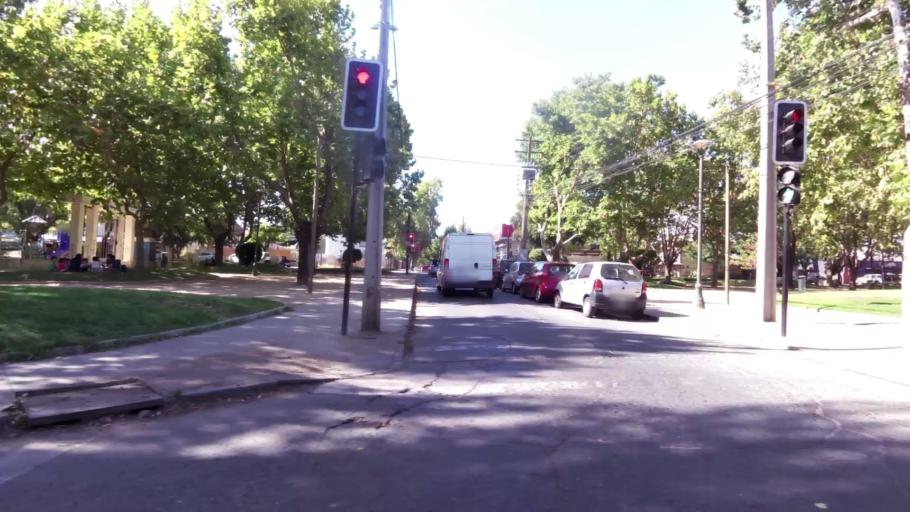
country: CL
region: Maule
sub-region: Provincia de Talca
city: Talca
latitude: -35.4225
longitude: -71.6608
